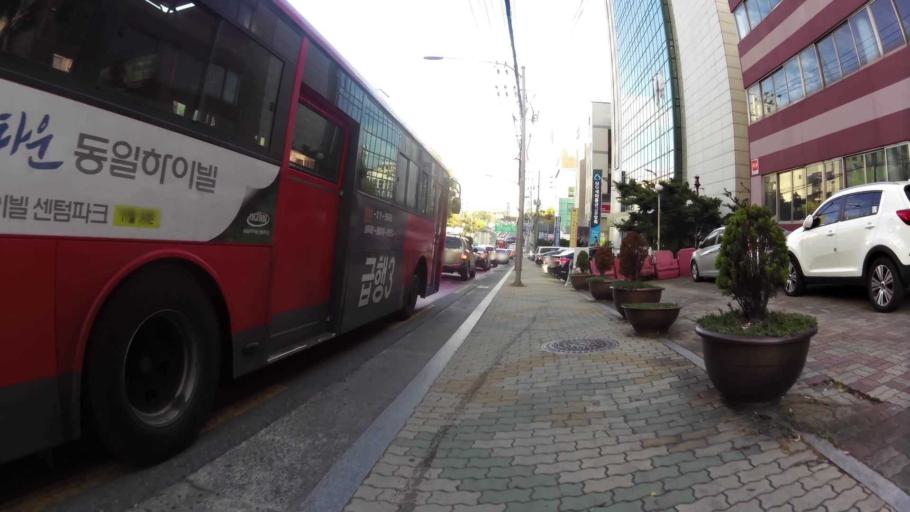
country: KR
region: Daegu
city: Daegu
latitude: 35.8672
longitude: 128.6249
